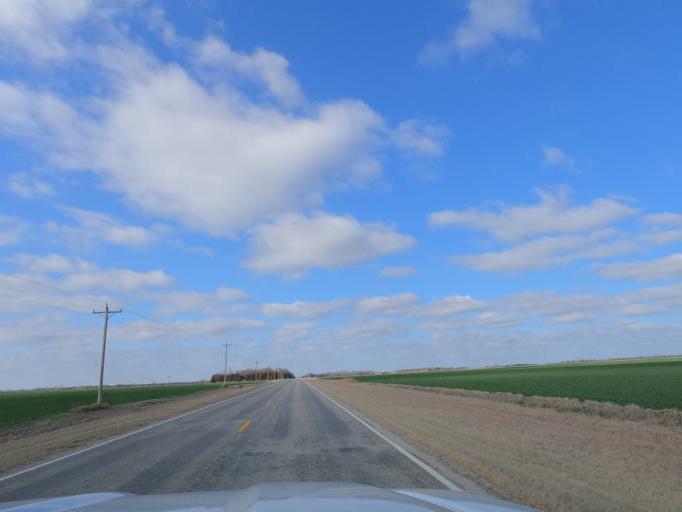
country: US
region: Kansas
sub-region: McPherson County
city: Inman
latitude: 38.1983
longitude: -97.8484
